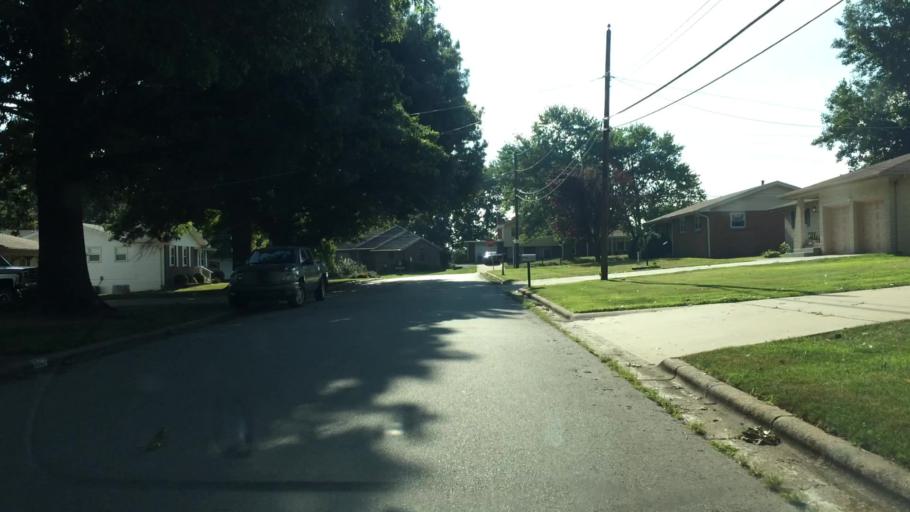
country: US
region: Missouri
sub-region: Greene County
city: Springfield
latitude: 37.2555
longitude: -93.2678
